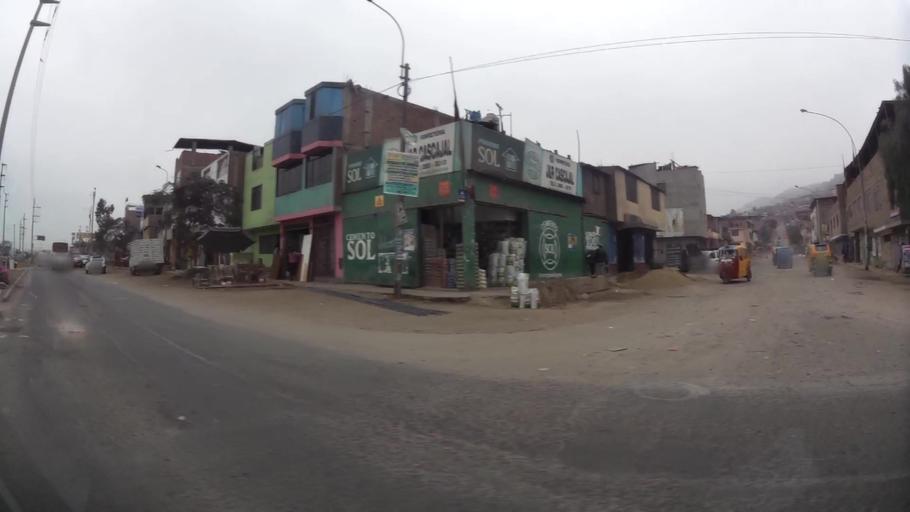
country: PE
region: Lima
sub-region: Lima
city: Surco
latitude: -12.1511
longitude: -76.9666
